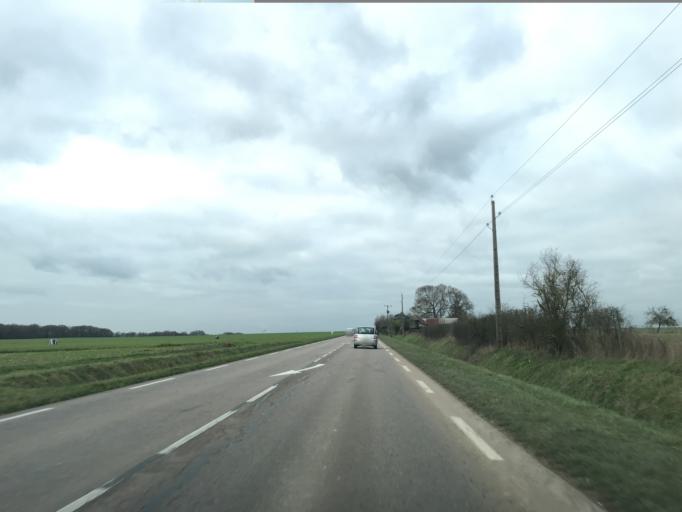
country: FR
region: Haute-Normandie
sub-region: Departement de l'Eure
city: Fleury-sur-Andelle
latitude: 49.3737
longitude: 1.3324
